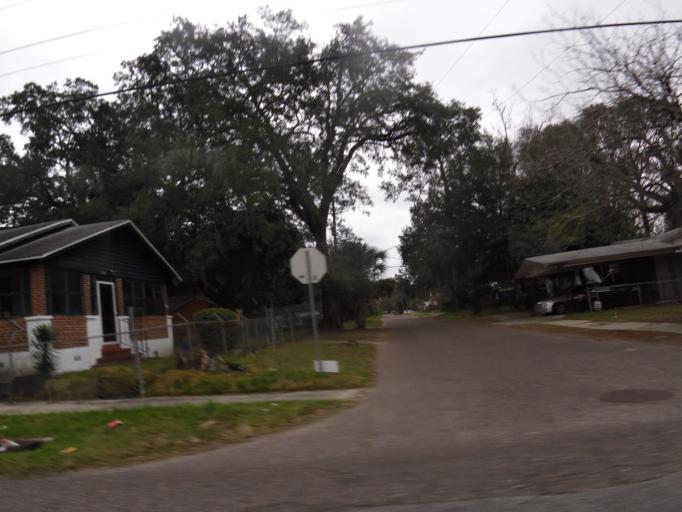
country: US
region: Florida
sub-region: Duval County
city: Jacksonville
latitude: 30.3636
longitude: -81.6848
